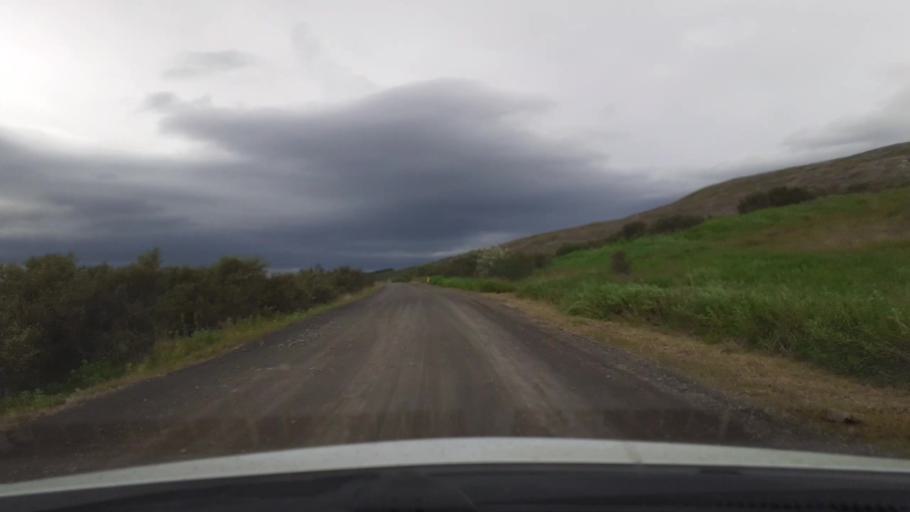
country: IS
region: Capital Region
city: Mosfellsbaer
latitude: 64.5248
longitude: -21.4773
